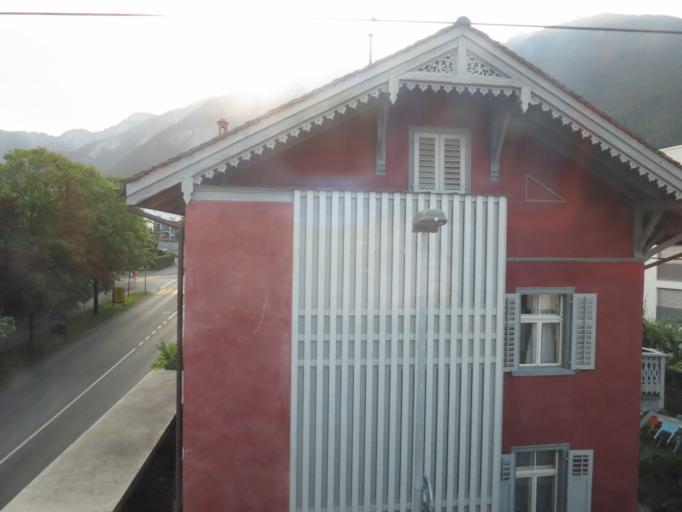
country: CH
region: Grisons
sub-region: Plessur District
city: Chur
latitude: 46.8606
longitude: 9.5318
